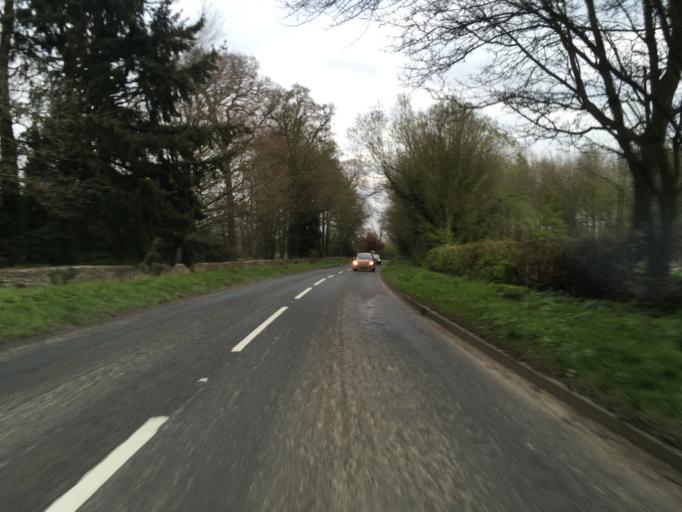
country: GB
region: England
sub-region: Gloucestershire
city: Northleach
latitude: 51.7478
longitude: -1.8798
